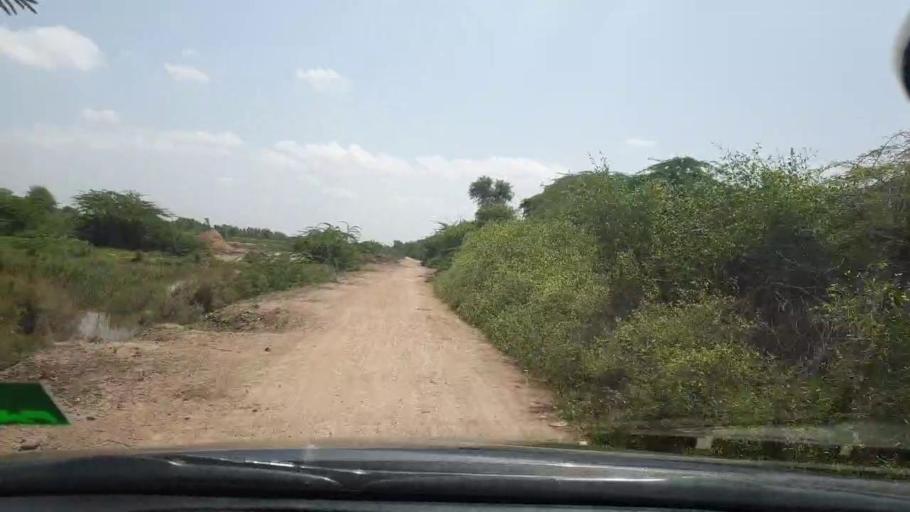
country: PK
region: Sindh
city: Tando Bago
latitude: 24.8546
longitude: 69.0890
